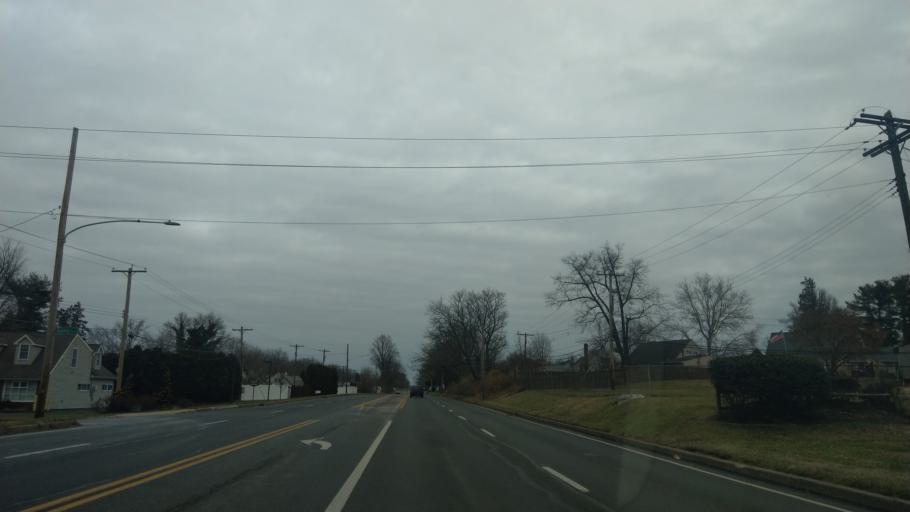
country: US
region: Pennsylvania
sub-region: Bucks County
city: Fairless Hills
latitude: 40.1436
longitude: -74.8713
